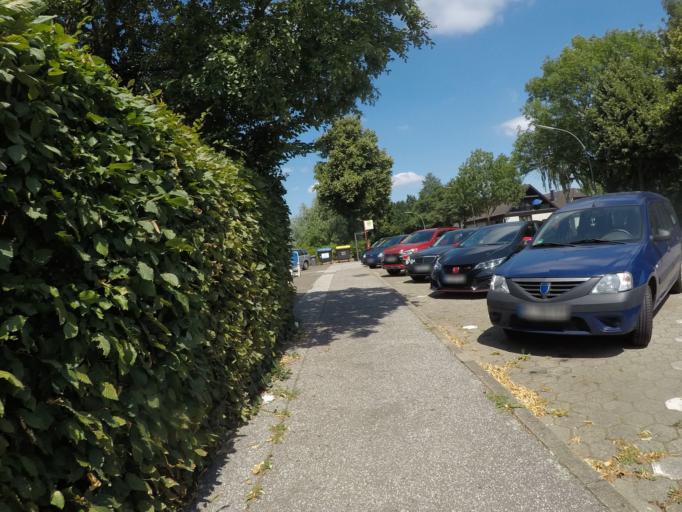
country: DE
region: Hamburg
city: Rothenburgsort
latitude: 53.4989
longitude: 10.0247
